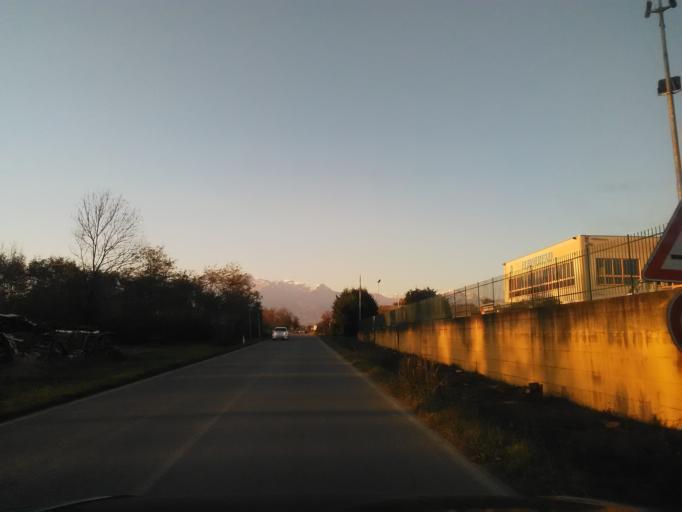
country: IT
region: Piedmont
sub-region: Provincia di Biella
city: Cerrione
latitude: 45.4814
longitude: 8.0730
